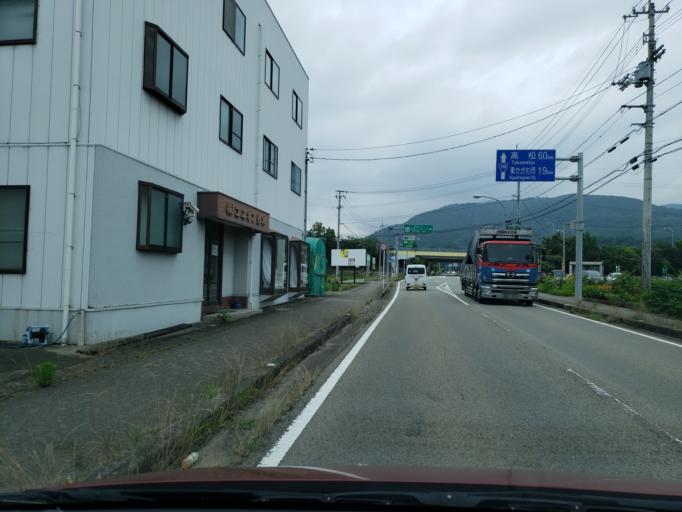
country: JP
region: Tokushima
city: Kamojimacho-jogejima
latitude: 34.1190
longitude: 134.3533
